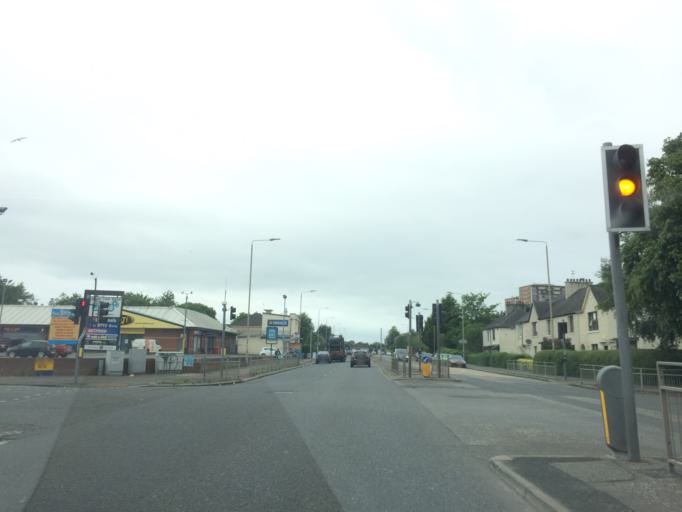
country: GB
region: Scotland
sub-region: East Dunbartonshire
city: Bearsden
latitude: 55.8551
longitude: -4.3295
